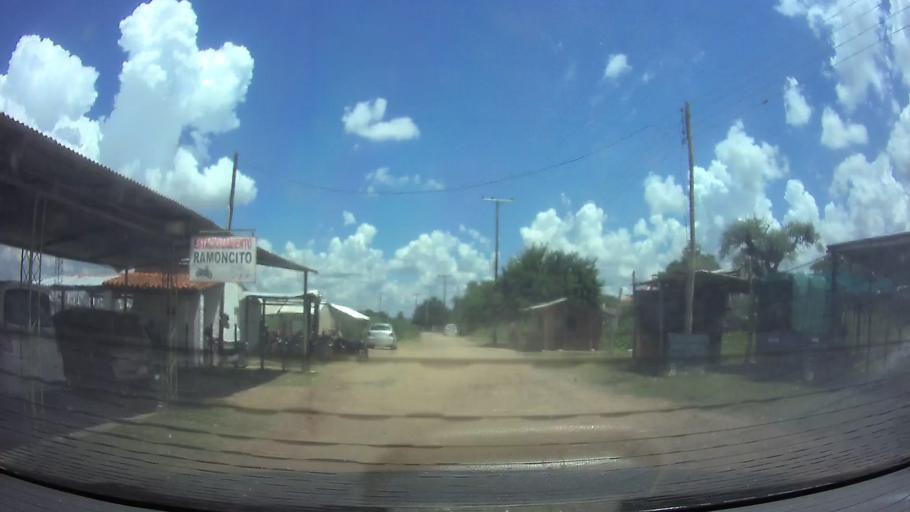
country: PY
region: Presidente Hayes
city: Nanawa
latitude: -25.2561
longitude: -57.6395
